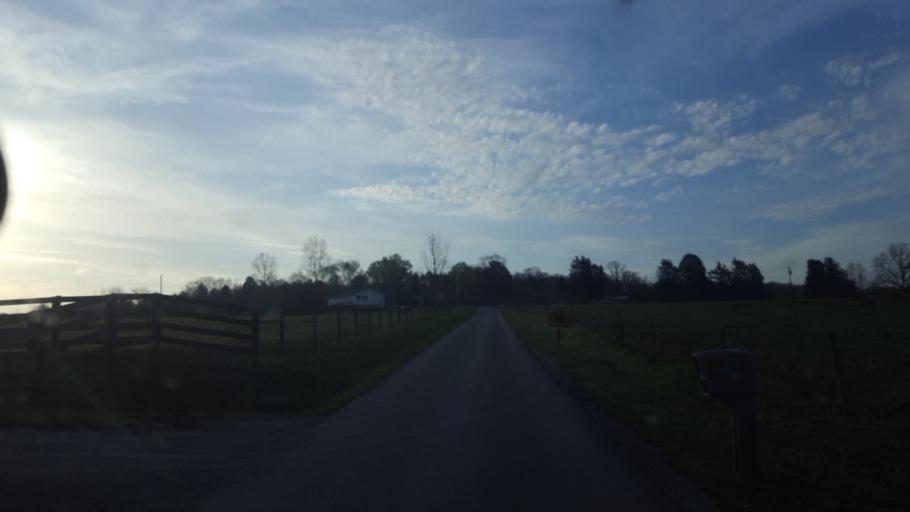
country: US
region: Kentucky
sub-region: Hart County
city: Horse Cave
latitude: 37.2233
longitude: -85.9644
